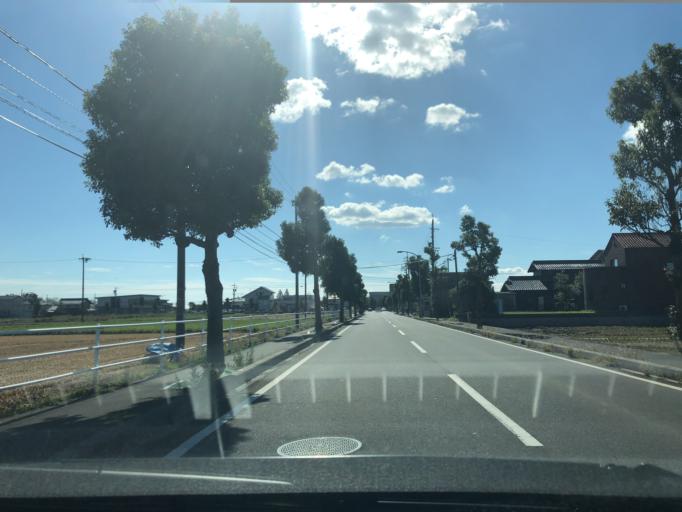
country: JP
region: Gifu
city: Godo
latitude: 35.4081
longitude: 136.6502
